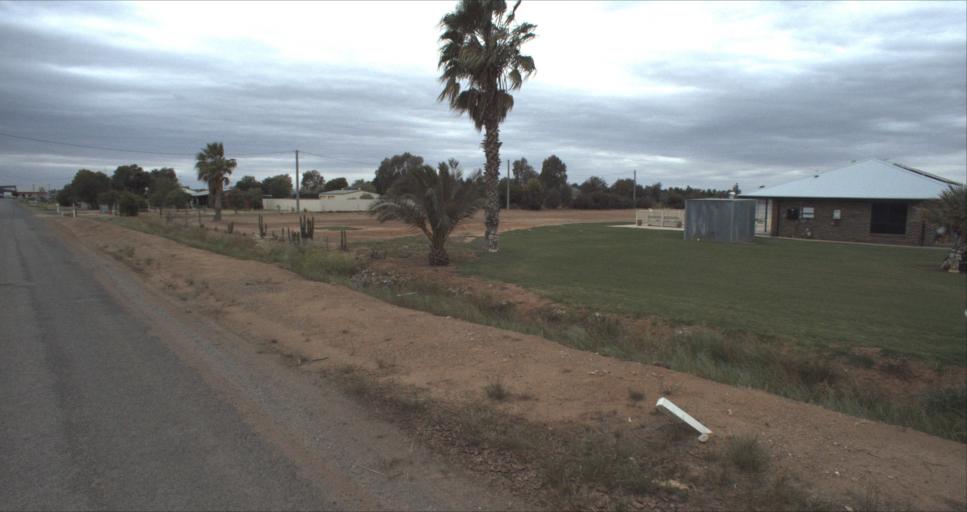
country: AU
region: New South Wales
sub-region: Leeton
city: Leeton
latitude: -34.5429
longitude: 146.3823
